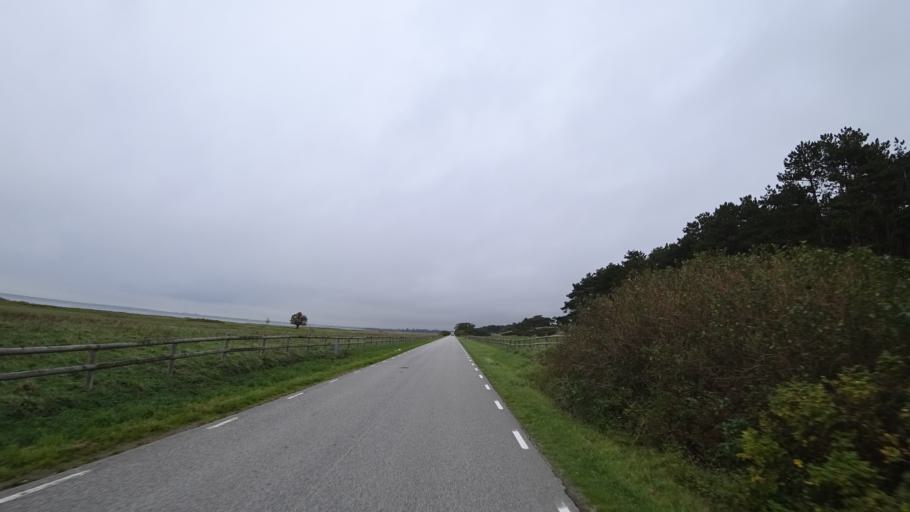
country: SE
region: Skane
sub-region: Kavlinge Kommun
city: Hofterup
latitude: 55.7904
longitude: 12.9383
